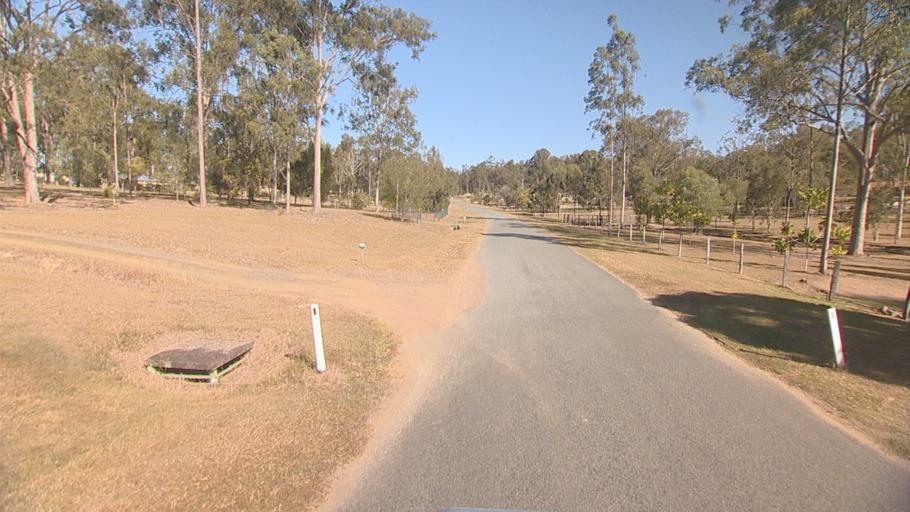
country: AU
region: Queensland
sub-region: Logan
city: Cedar Vale
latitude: -27.8590
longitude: 153.0337
